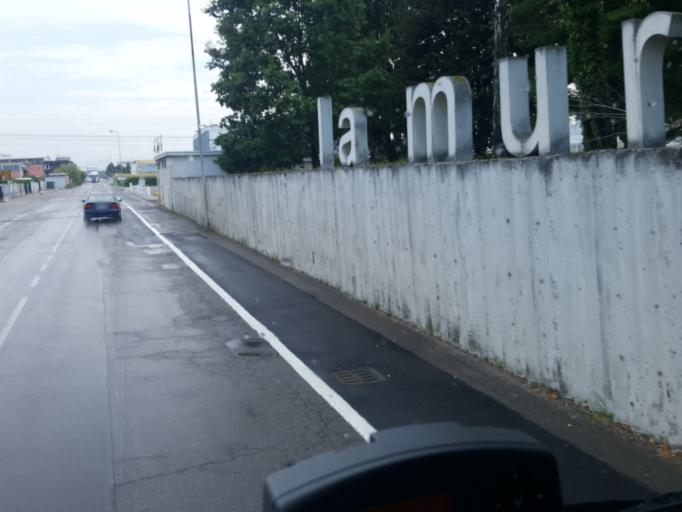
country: IT
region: Lombardy
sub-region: Provincia di Como
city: Turate
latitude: 45.6599
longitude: 9.0180
